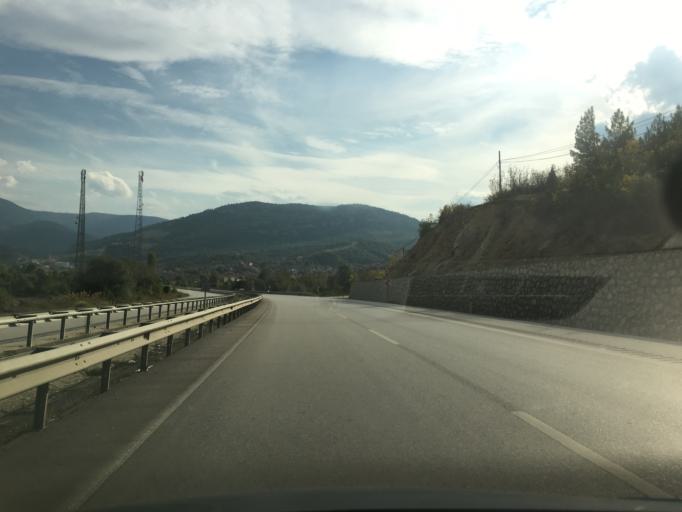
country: TR
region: Karabuk
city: Karabuk
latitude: 41.1113
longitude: 32.6693
